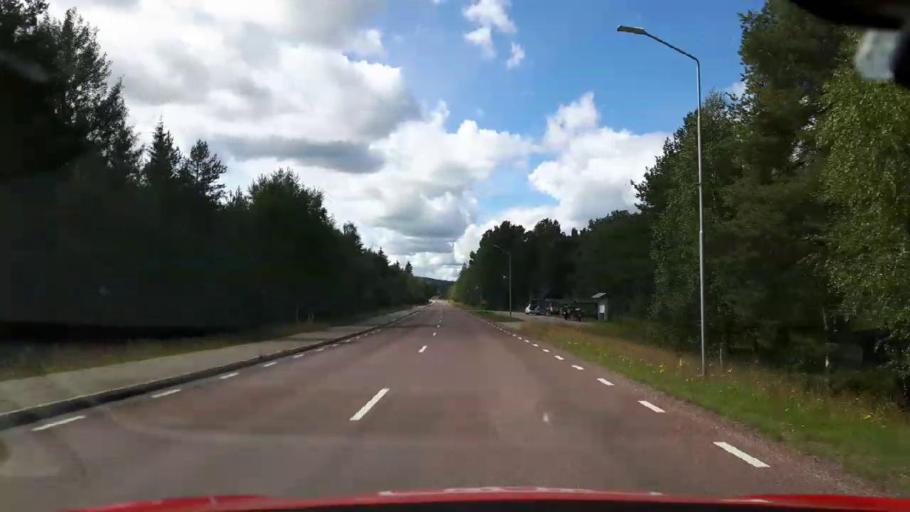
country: SE
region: Jaemtland
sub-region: Harjedalens Kommun
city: Sveg
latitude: 61.8562
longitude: 14.0908
